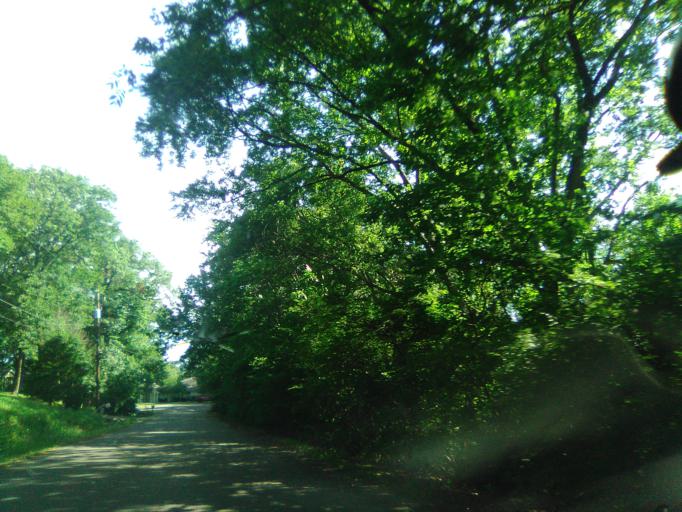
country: US
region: Tennessee
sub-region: Davidson County
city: Belle Meade
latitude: 36.1223
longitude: -86.9068
